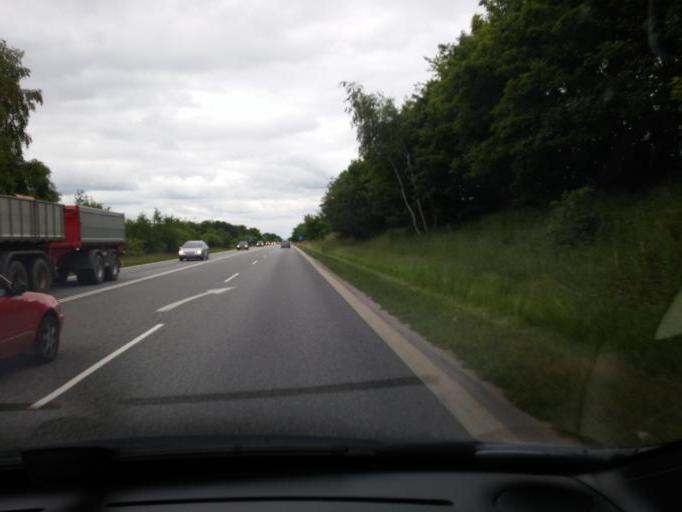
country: DK
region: Capital Region
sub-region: Hillerod Kommune
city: Hillerod
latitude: 55.9261
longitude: 12.2552
